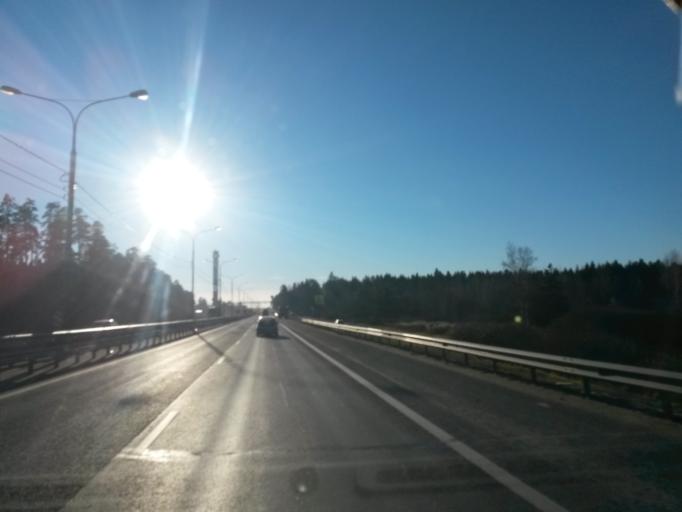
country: RU
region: Moskovskaya
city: Zelenogradskiy
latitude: 56.0949
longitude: 37.9400
